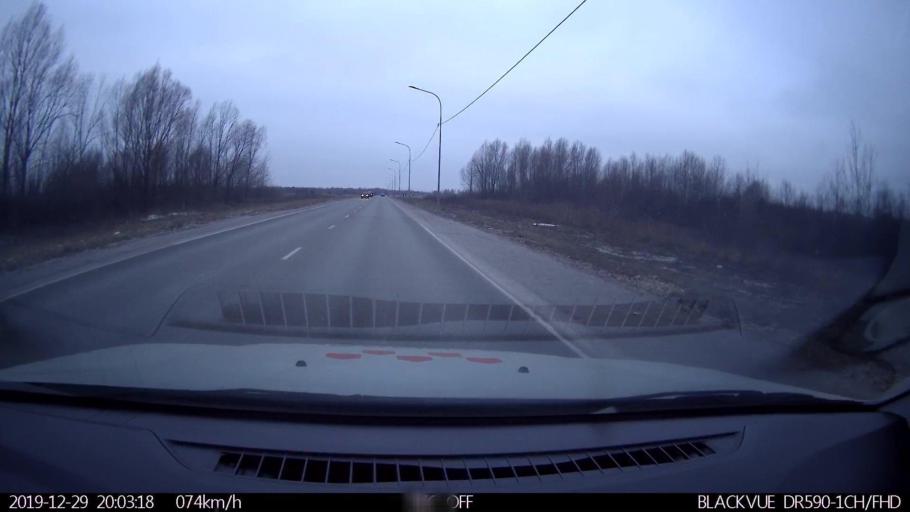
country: RU
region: Nizjnij Novgorod
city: Nizhniy Novgorod
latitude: 56.3732
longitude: 44.0200
